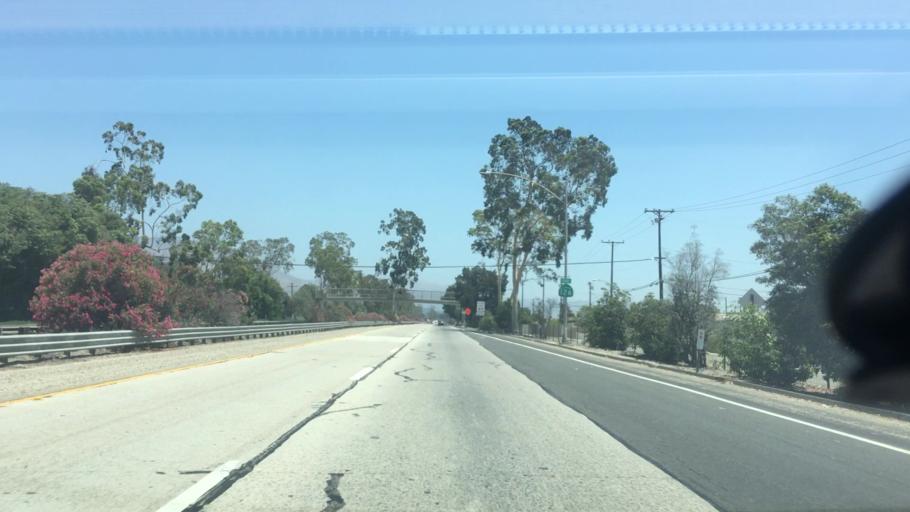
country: US
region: California
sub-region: Ventura County
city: Santa Paula
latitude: 34.3380
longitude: -119.0813
